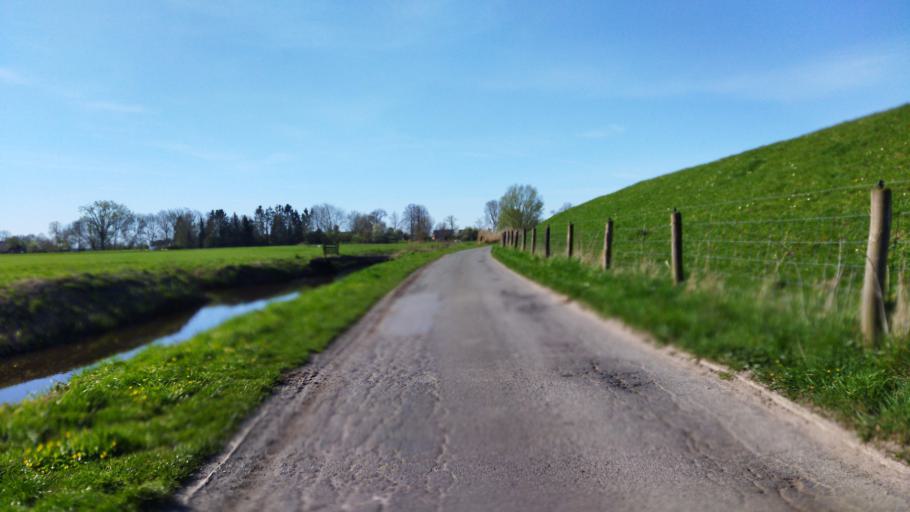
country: DE
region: Lower Saxony
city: Elsfleth
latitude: 53.2029
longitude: 8.4532
